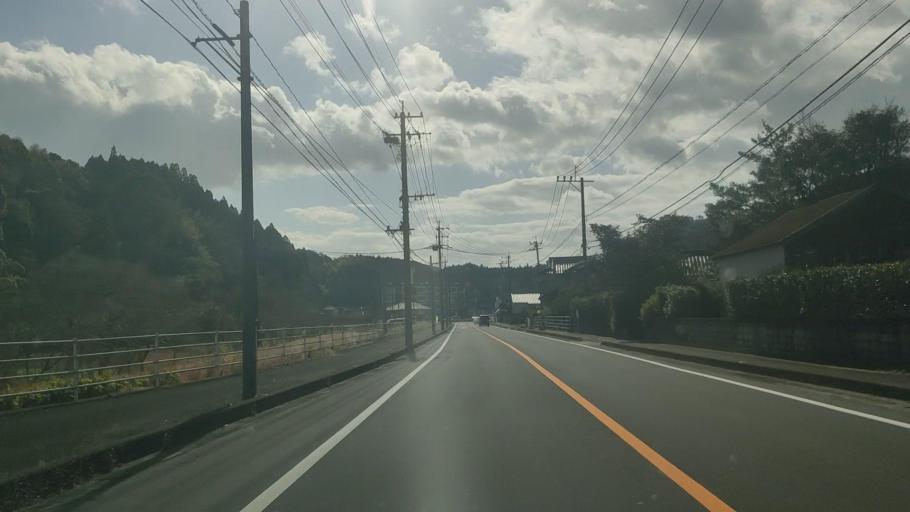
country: JP
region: Kagoshima
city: Okuchi-shinohara
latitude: 31.9447
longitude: 130.7109
